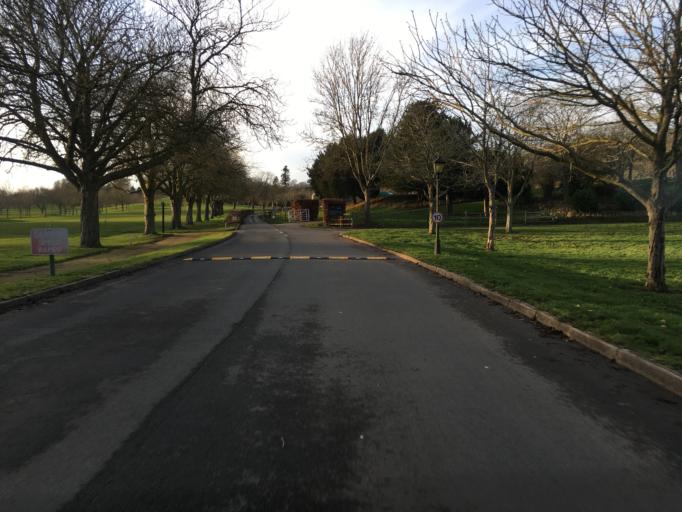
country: GB
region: England
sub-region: Warwickshire
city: Stratford-upon-Avon
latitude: 52.2071
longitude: -1.6858
